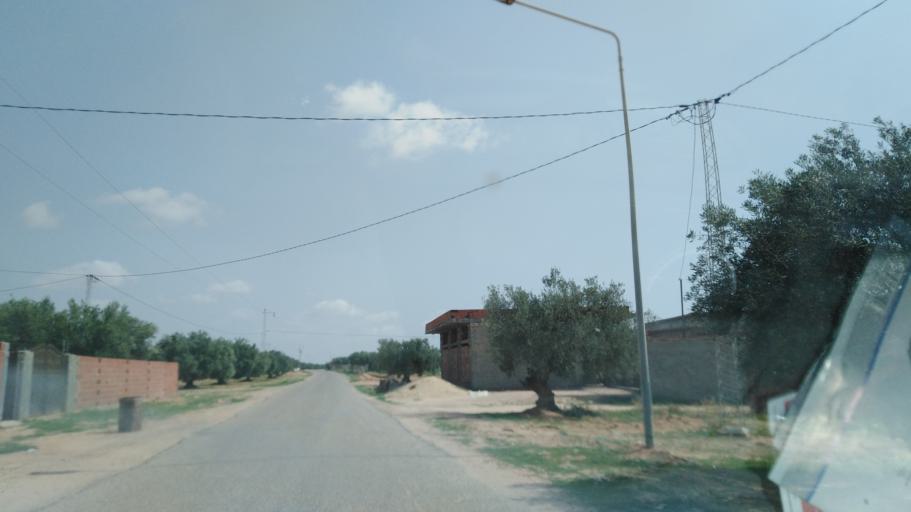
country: TN
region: Safaqis
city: Sfax
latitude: 34.6306
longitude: 10.6015
